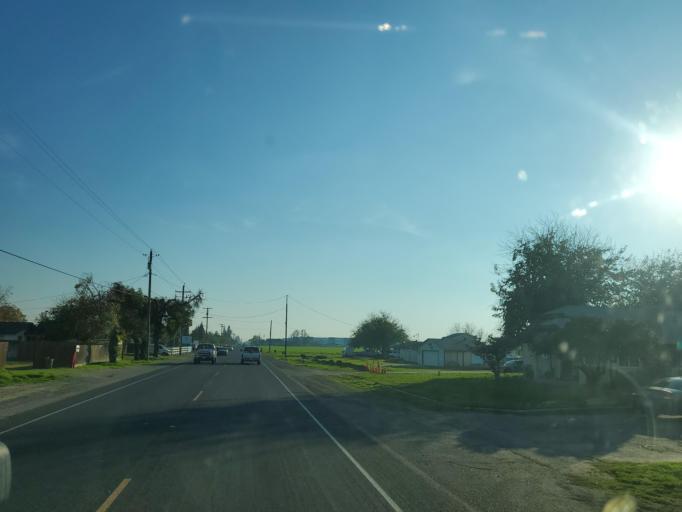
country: US
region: California
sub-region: San Joaquin County
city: French Camp
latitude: 37.8629
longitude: -121.2559
